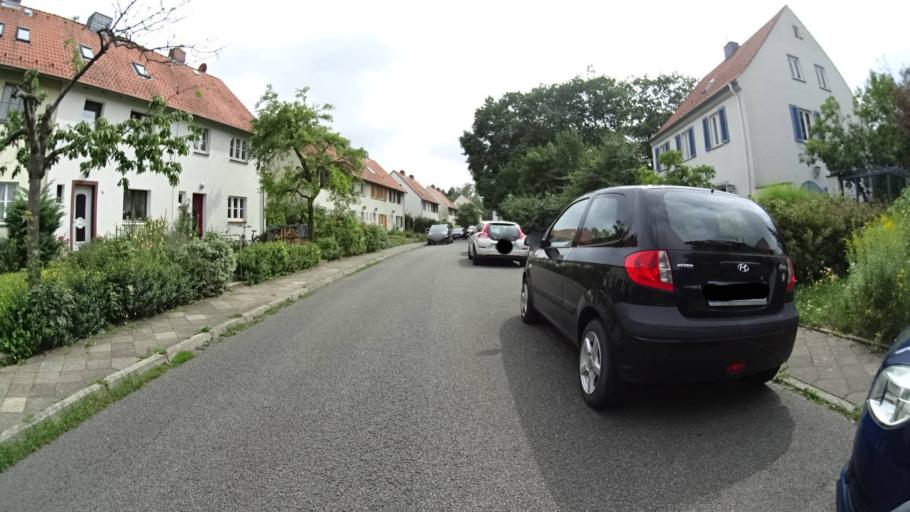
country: DE
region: Lower Saxony
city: Lueneburg
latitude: 53.2379
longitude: 10.4062
